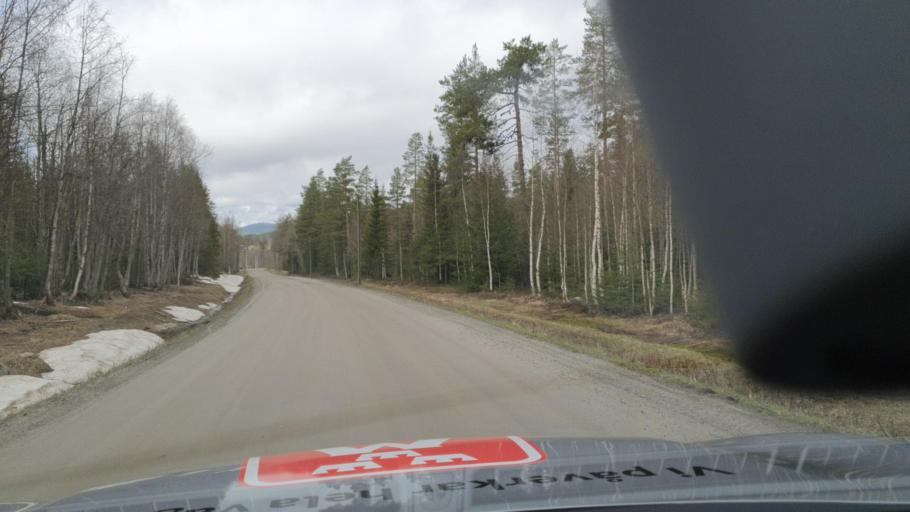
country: SE
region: Vaesterbotten
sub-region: Bjurholms Kommun
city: Bjurholm
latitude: 63.6844
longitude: 18.9722
